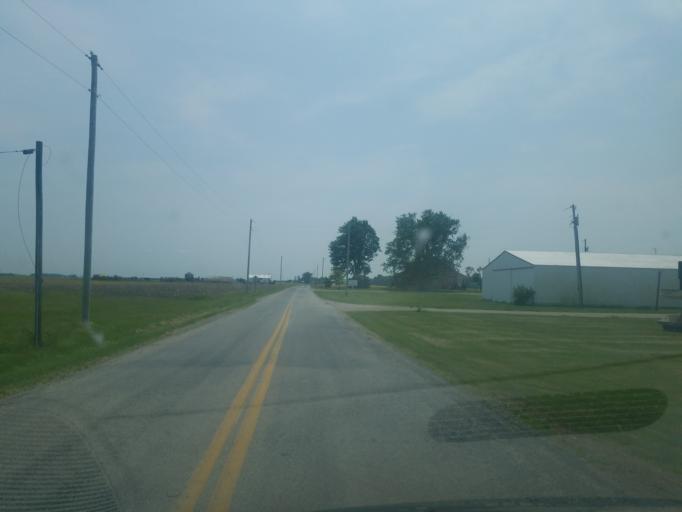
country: US
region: Ohio
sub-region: Wyandot County
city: Upper Sandusky
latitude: 40.6936
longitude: -83.2989
